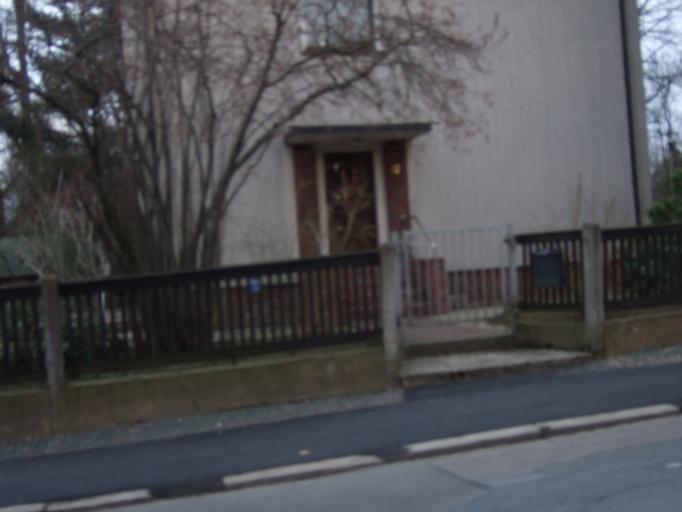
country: DE
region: Saxony
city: Freiberg
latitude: 50.9151
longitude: 13.3298
